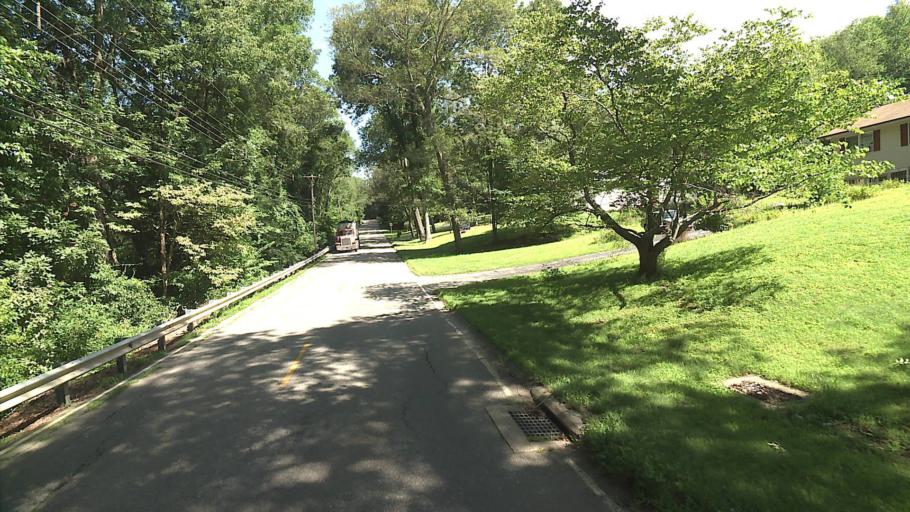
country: US
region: Connecticut
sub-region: New London County
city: Baltic
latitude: 41.6297
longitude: -72.0854
